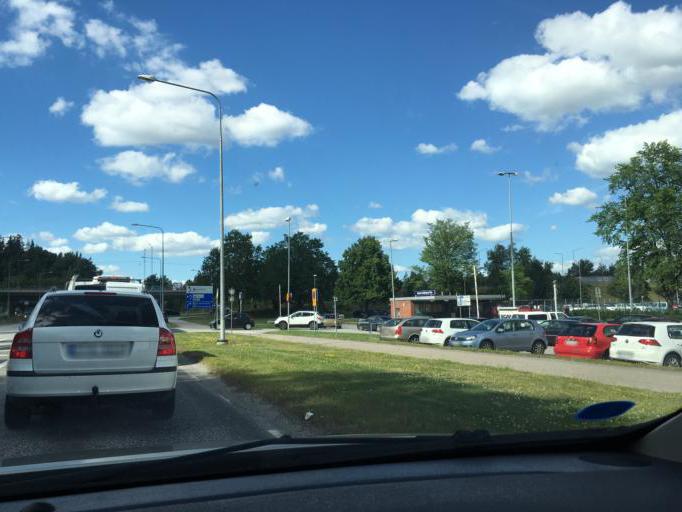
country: SE
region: Stockholm
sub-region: Sodertalje Kommun
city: Soedertaelje
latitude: 59.1748
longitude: 17.6347
